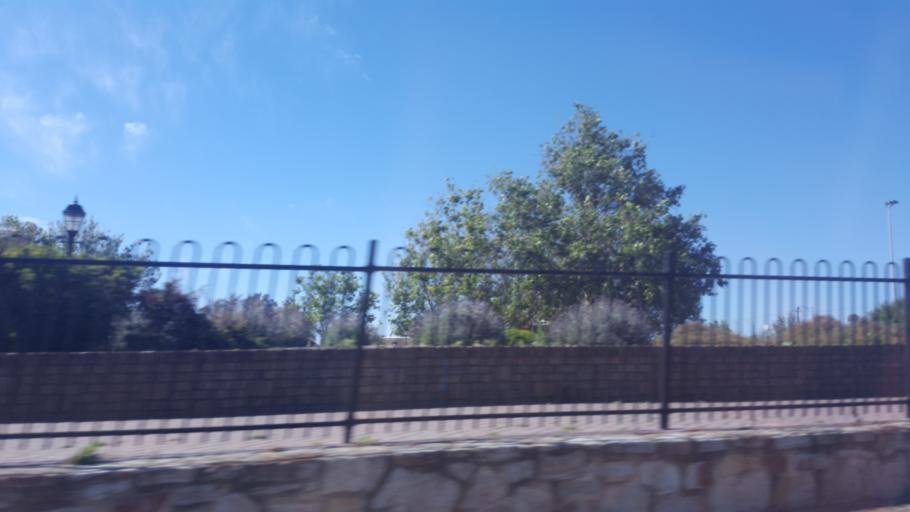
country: AU
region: South Australia
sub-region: Port Adelaide Enfield
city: Birkenhead
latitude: -34.8495
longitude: 138.5028
